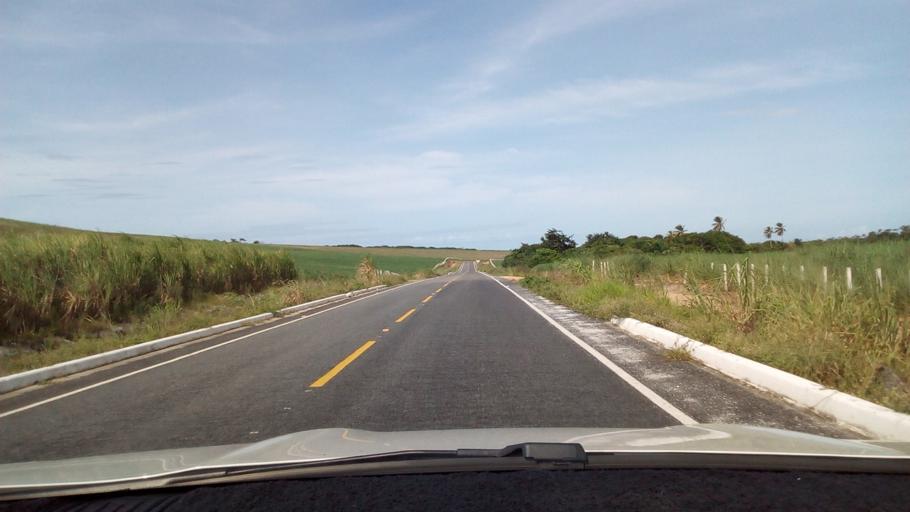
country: BR
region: Paraiba
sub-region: Joao Pessoa
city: Joao Pessoa
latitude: -7.0463
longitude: -34.8929
